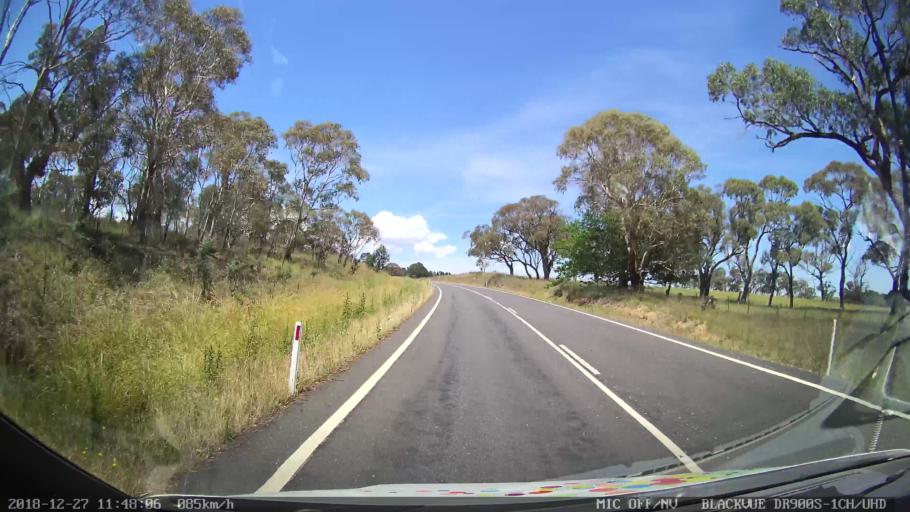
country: AU
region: New South Wales
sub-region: Bathurst Regional
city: Perthville
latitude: -33.6021
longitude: 149.4376
